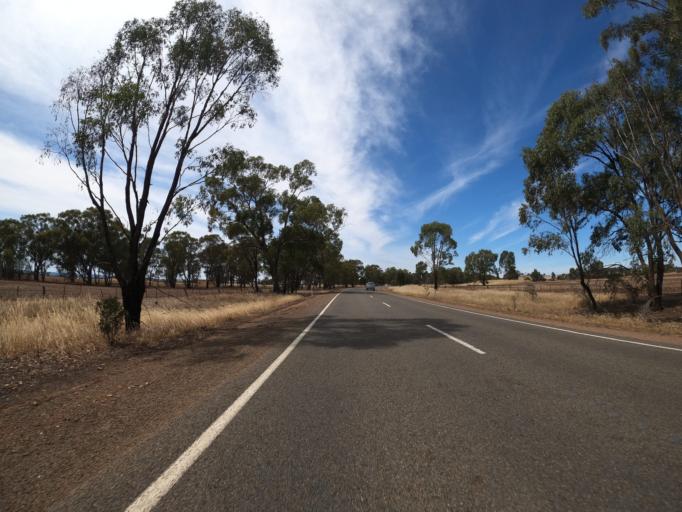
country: AU
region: Victoria
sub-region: Benalla
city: Benalla
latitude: -36.3054
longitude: 145.9573
